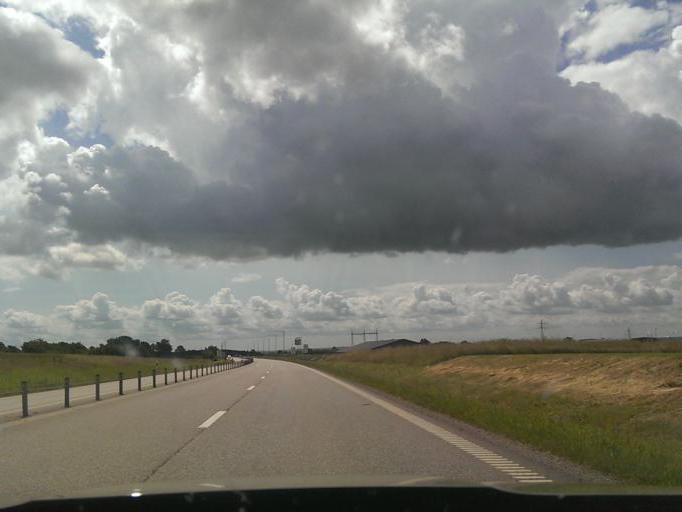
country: SE
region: Skane
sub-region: Eslovs Kommun
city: Eslov
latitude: 55.8304
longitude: 13.3322
